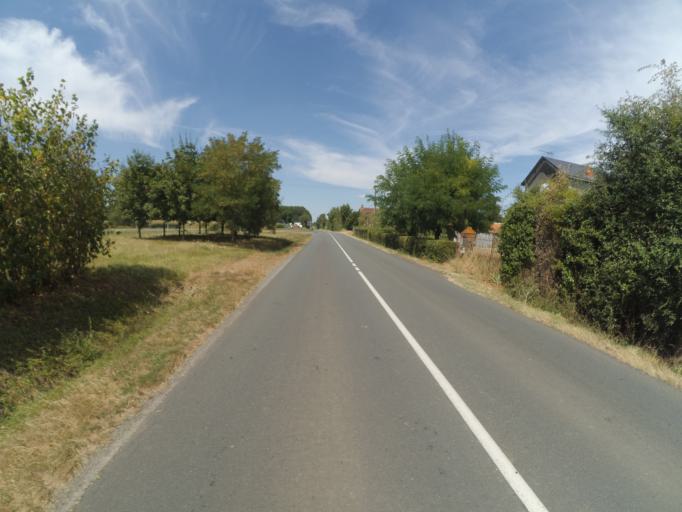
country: FR
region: Poitou-Charentes
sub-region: Departement de la Vienne
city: Usson-du-Poitou
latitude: 46.2746
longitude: 0.5184
